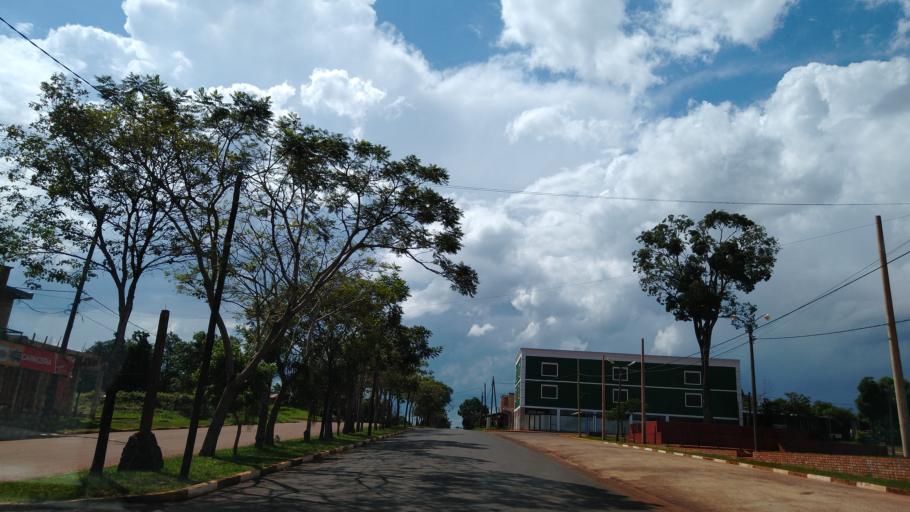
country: AR
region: Misiones
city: Puerto Libertad
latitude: -25.9652
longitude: -54.5604
